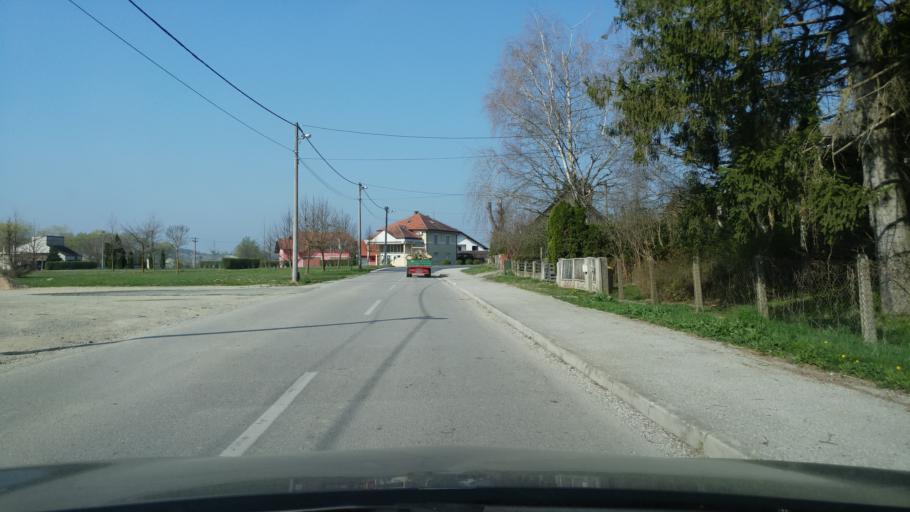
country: HR
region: Zagrebacka
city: Pojatno
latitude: 45.9527
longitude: 15.7344
